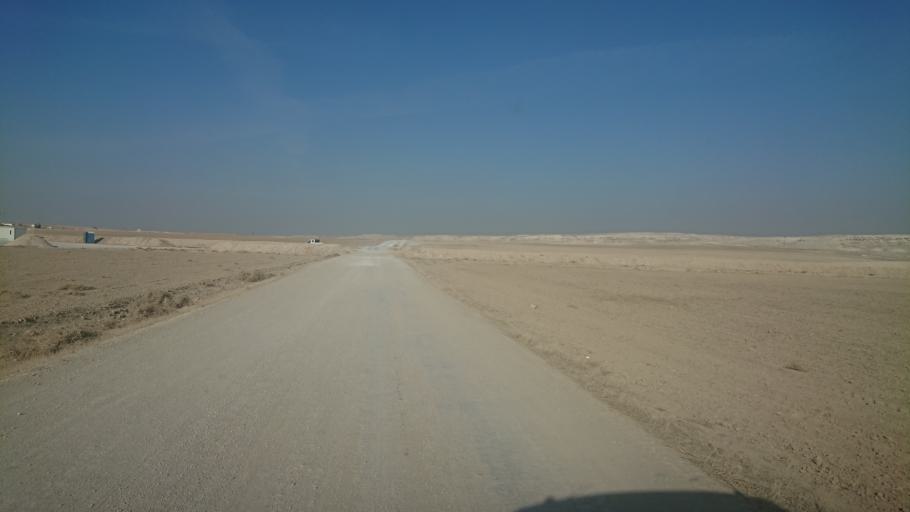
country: TR
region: Aksaray
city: Sultanhani
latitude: 38.0668
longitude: 33.6159
